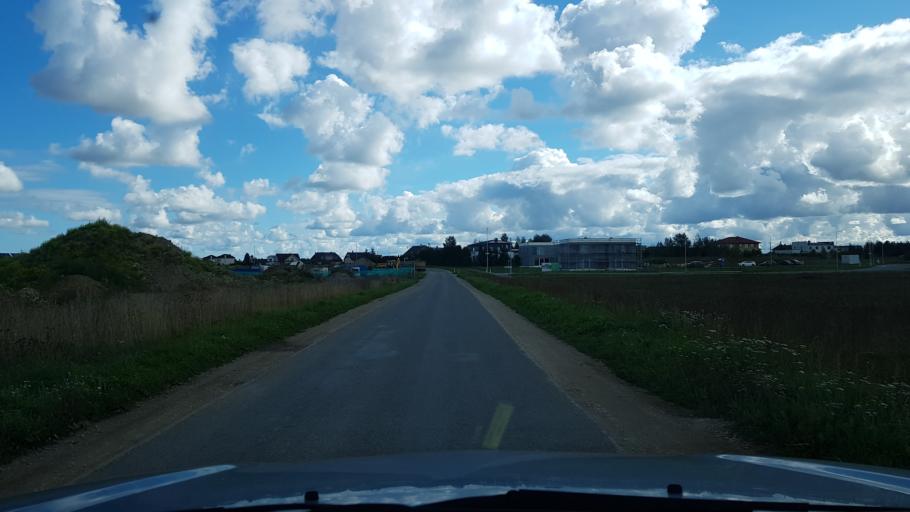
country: EE
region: Harju
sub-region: Tallinna linn
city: Tallinn
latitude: 59.3821
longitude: 24.8055
